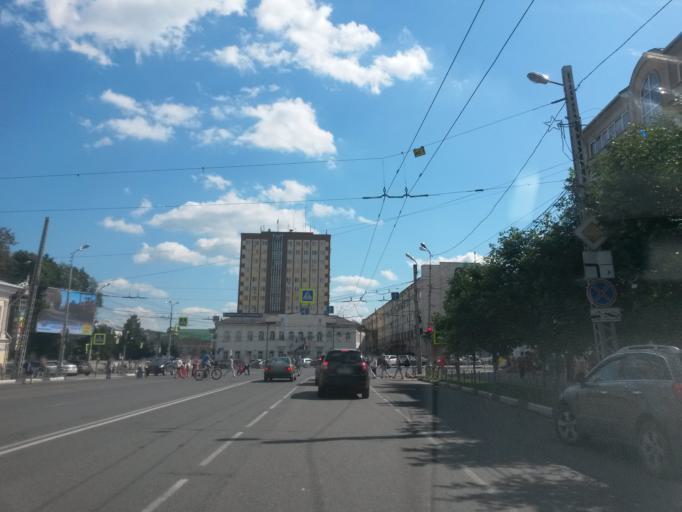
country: RU
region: Ivanovo
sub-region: Gorod Ivanovo
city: Ivanovo
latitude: 56.9961
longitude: 40.9780
